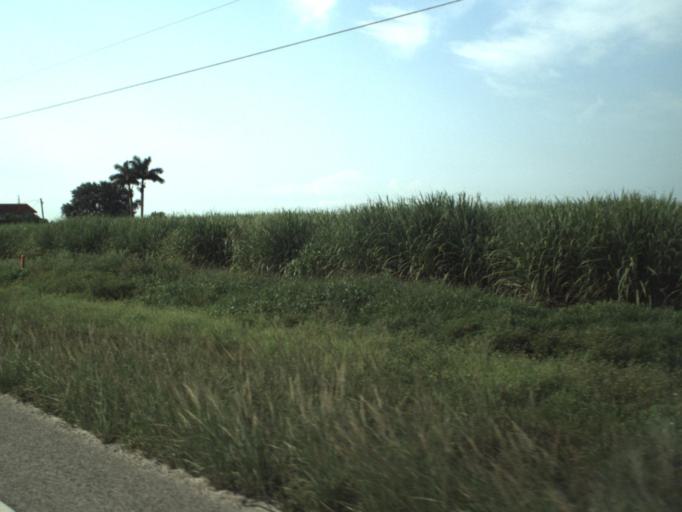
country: US
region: Florida
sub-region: Hendry County
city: Clewiston
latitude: 26.7136
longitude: -80.8379
